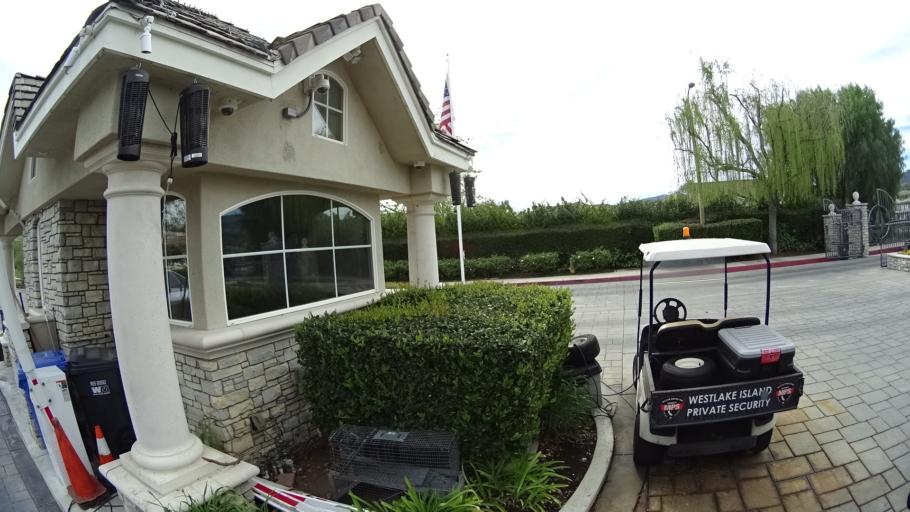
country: US
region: California
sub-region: Los Angeles County
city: Westlake Village
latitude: 34.1458
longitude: -118.8257
